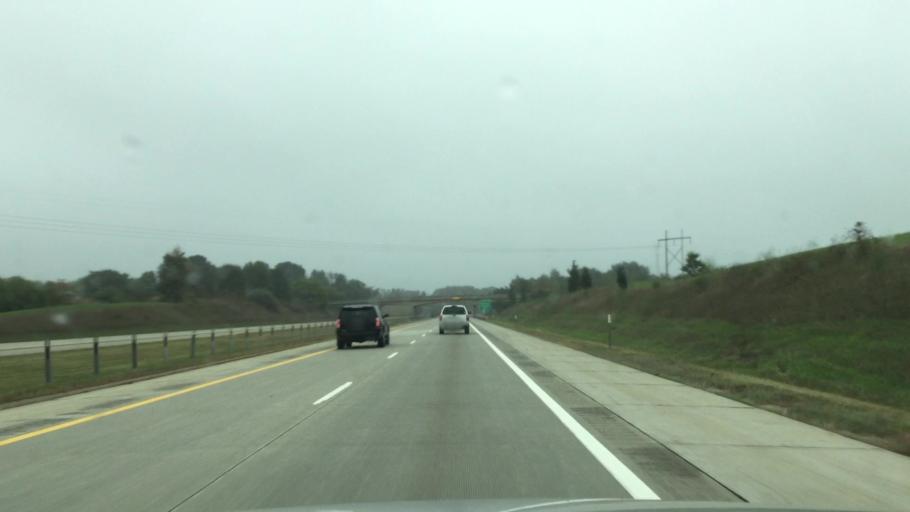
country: US
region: Michigan
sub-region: Berrien County
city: Coloma
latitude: 42.1679
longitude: -86.3229
